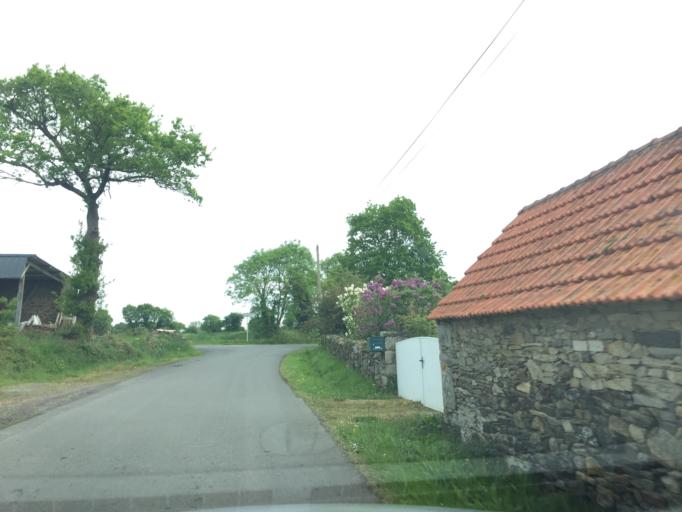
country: FR
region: Brittany
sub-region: Departement des Cotes-d'Armor
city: Saint-Cast-le-Guildo
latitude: 48.5984
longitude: -2.2342
